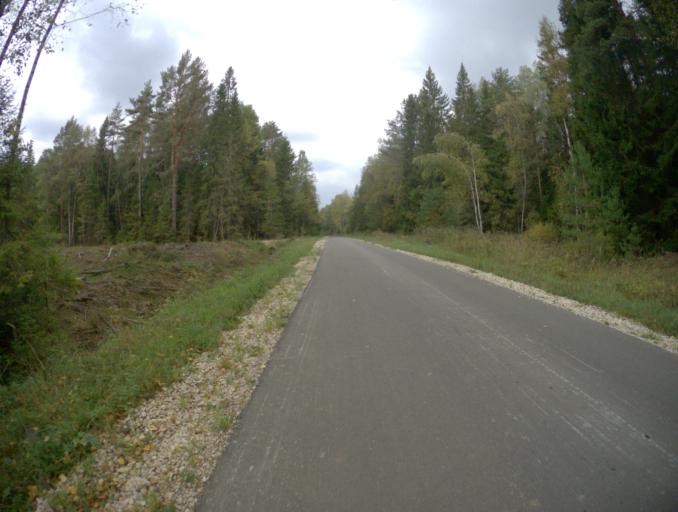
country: RU
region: Vladimir
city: Kideksha
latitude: 56.4741
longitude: 40.6655
